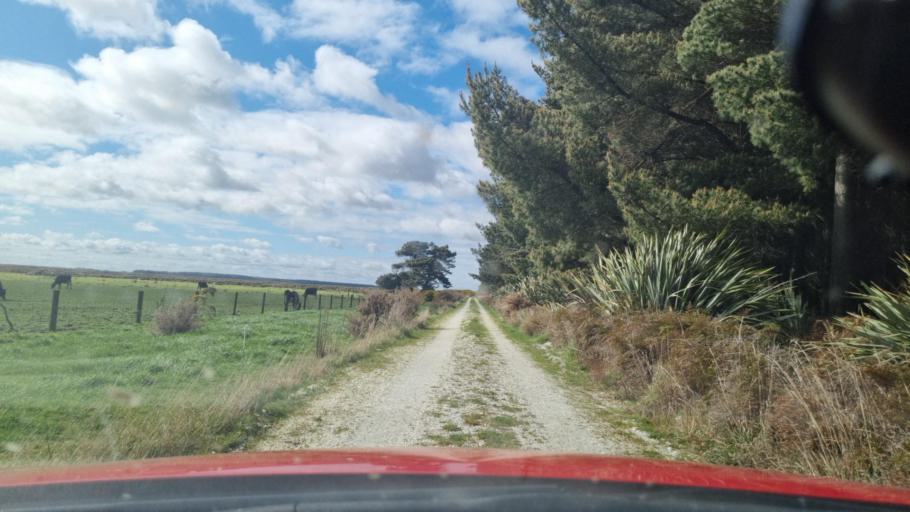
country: NZ
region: Southland
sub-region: Invercargill City
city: Invercargill
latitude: -46.4919
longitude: 168.4425
